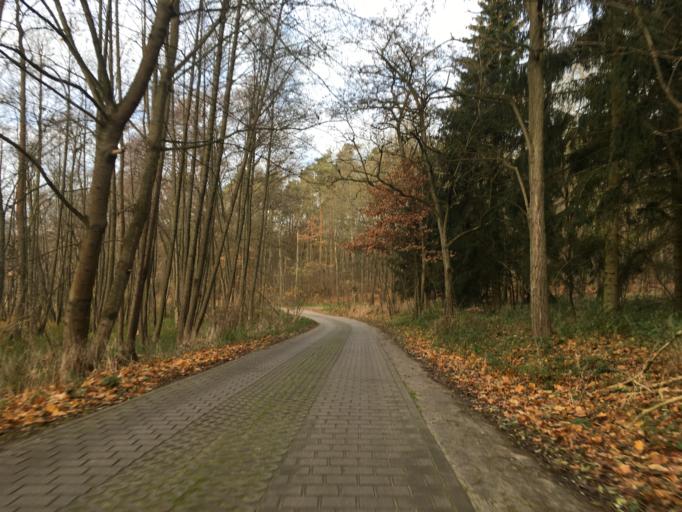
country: DE
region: Brandenburg
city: Buckow
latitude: 52.5665
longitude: 14.1225
